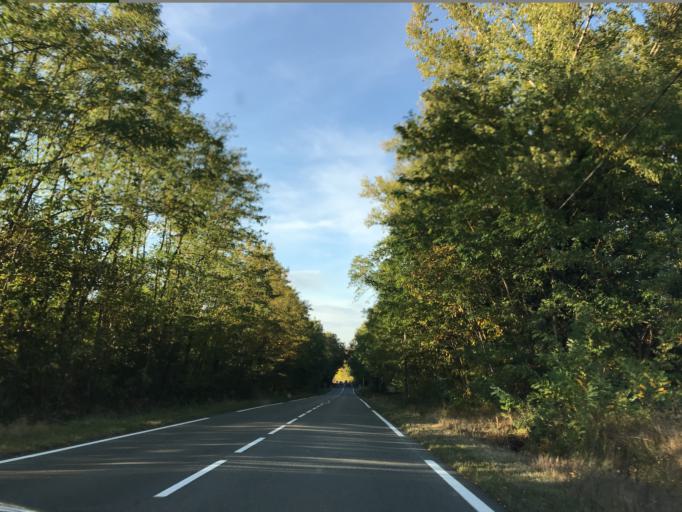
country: FR
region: Auvergne
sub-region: Departement du Puy-de-Dome
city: Paslieres
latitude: 45.9415
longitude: 3.4856
